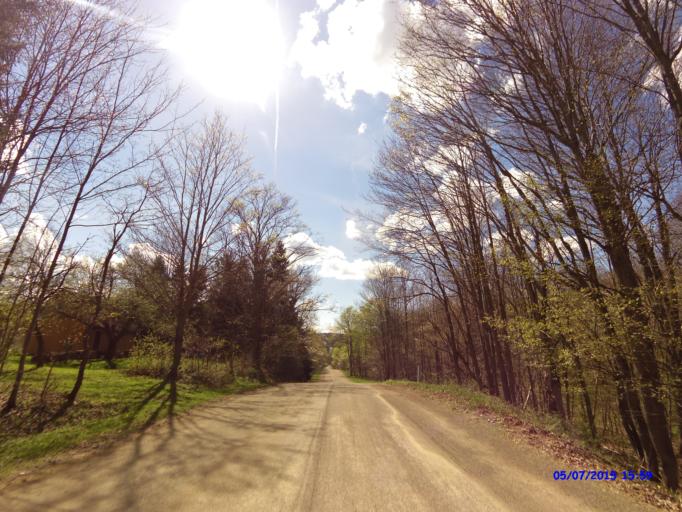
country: US
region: New York
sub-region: Cattaraugus County
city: Franklinville
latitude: 42.2982
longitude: -78.5863
